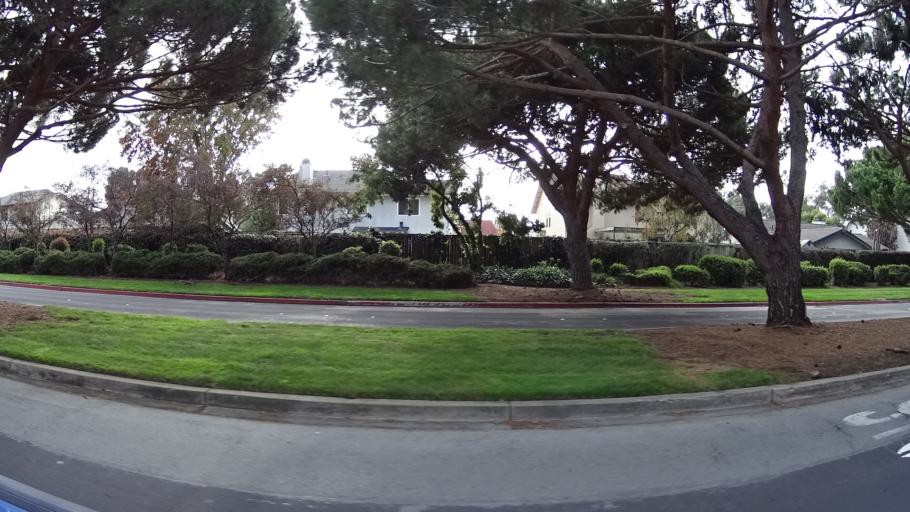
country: US
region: California
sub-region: San Mateo County
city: Redwood Shores
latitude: 37.5346
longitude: -122.2434
